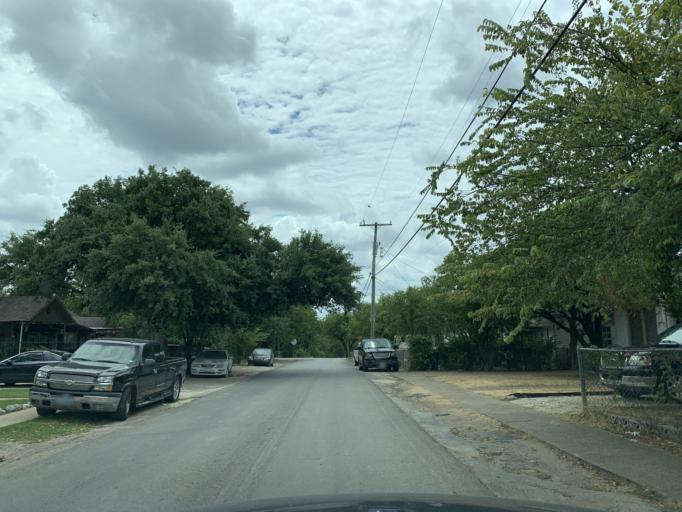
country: US
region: Texas
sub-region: Dallas County
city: Cockrell Hill
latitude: 32.7488
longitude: -96.8783
